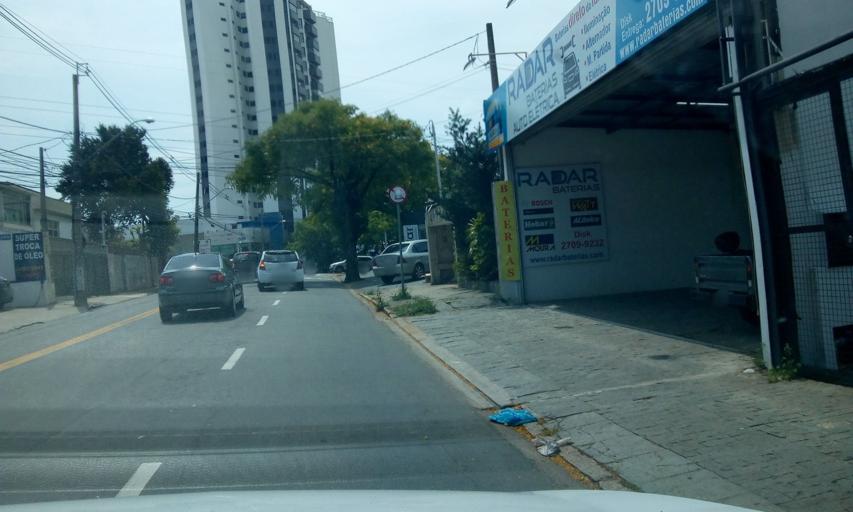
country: BR
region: Sao Paulo
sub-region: Jundiai
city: Jundiai
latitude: -23.2035
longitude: -46.8902
